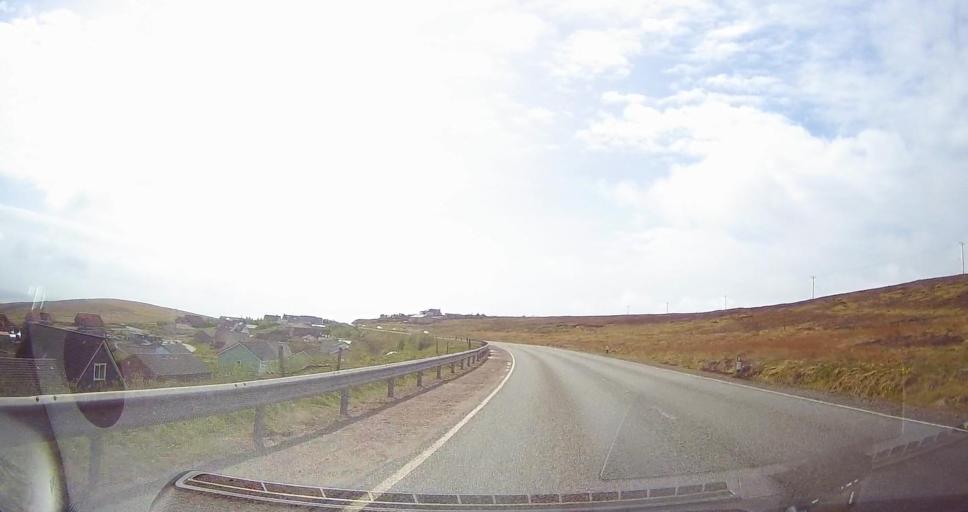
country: GB
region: Scotland
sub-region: Shetland Islands
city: Lerwick
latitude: 60.1258
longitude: -1.2162
